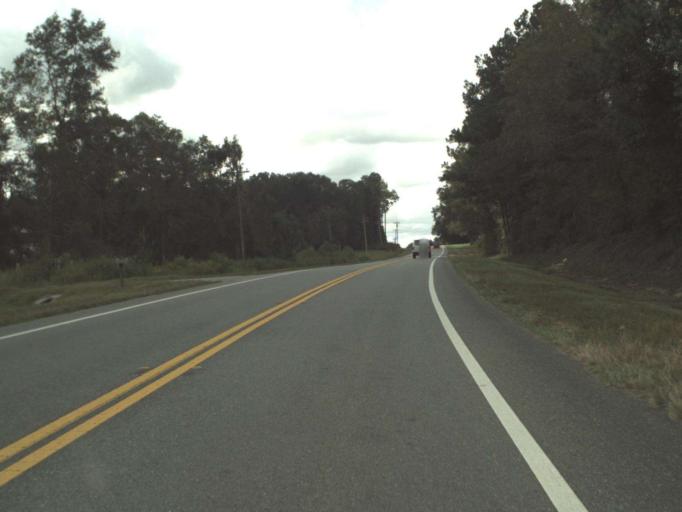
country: US
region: Florida
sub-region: Washington County
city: Chipley
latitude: 30.8172
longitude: -85.5058
